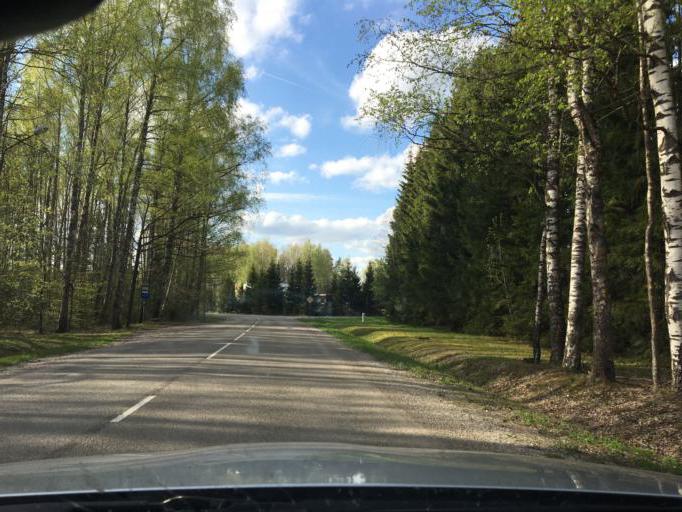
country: LV
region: Ozolnieku
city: Ozolnieki
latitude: 56.6860
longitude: 23.8321
